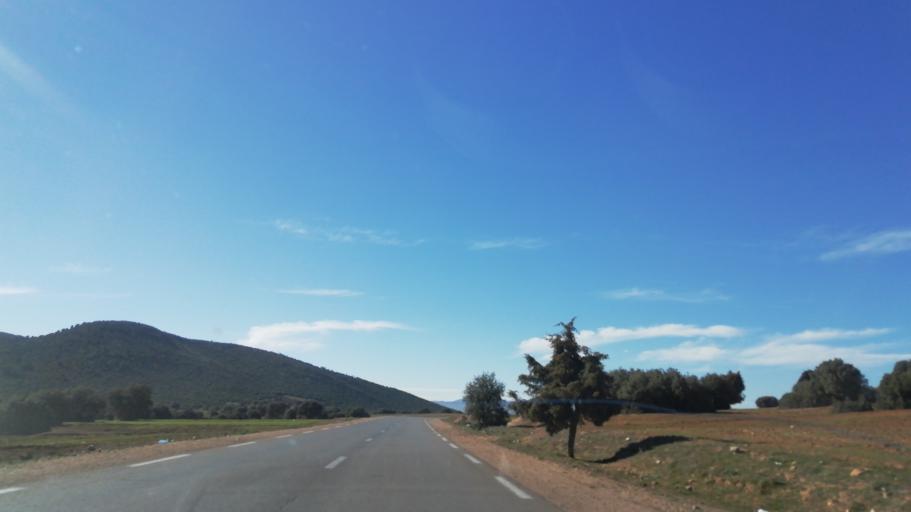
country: DZ
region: Tlemcen
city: Sebdou
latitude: 34.7066
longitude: -1.2164
